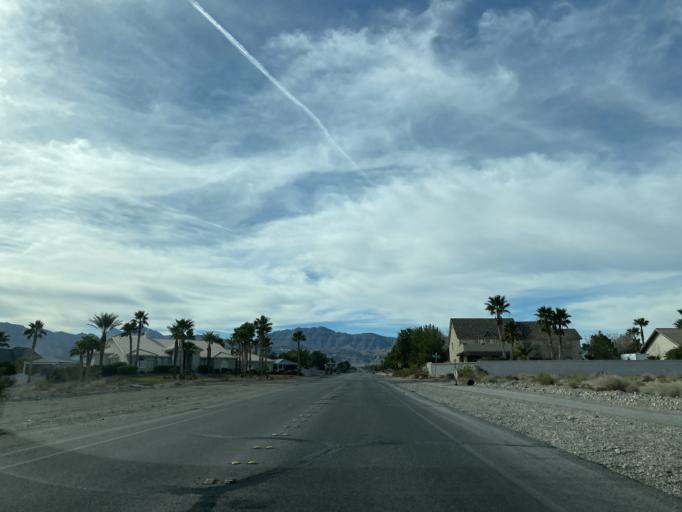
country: US
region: Nevada
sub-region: Clark County
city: Summerlin South
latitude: 36.2700
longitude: -115.2987
